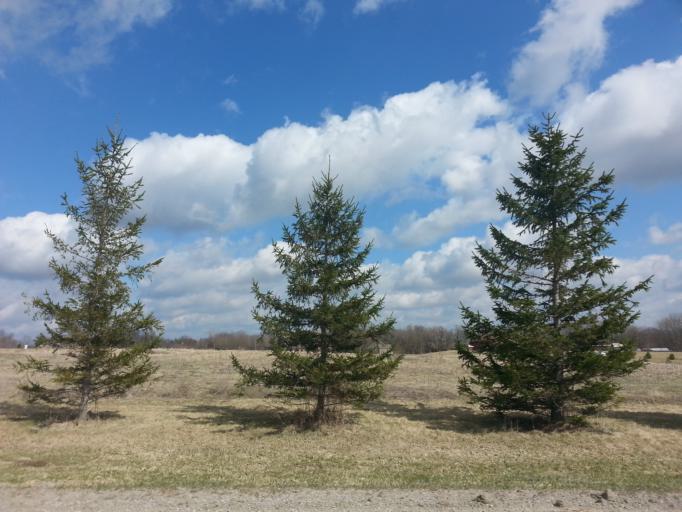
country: US
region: Minnesota
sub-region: Dodge County
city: Mantorville
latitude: 44.0702
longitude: -92.7183
